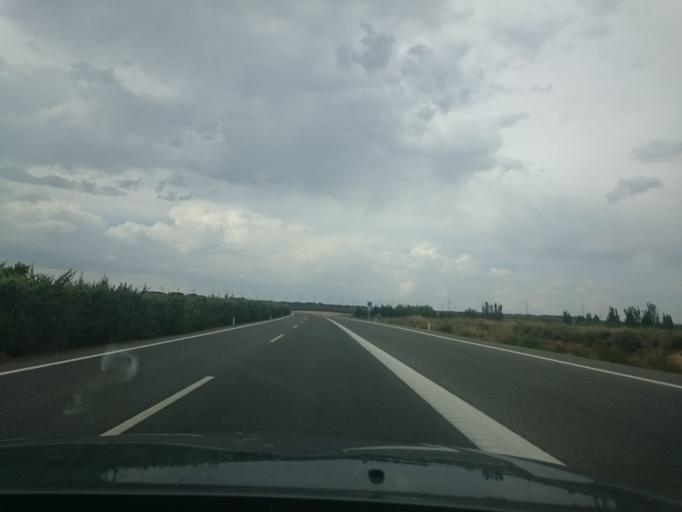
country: ES
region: Navarre
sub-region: Provincia de Navarra
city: Murchante
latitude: 42.0671
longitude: -1.6903
